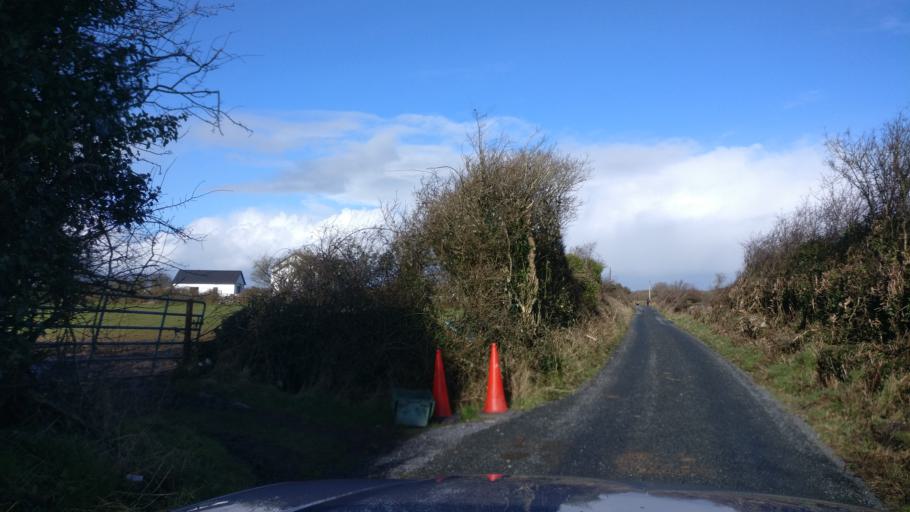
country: IE
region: Connaught
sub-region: County Galway
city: Athenry
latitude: 53.2388
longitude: -8.7746
